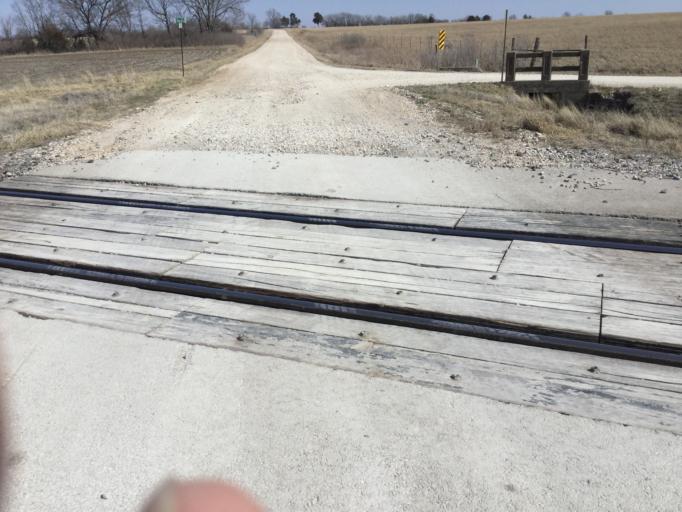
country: US
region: Kansas
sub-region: Woodson County
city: Yates Center
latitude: 37.6973
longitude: -95.7117
